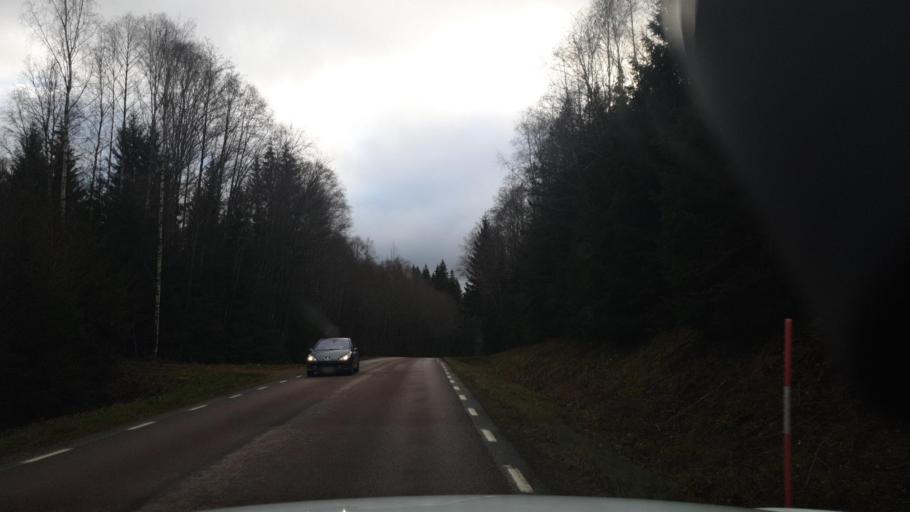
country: SE
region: Vaermland
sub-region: Arvika Kommun
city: Arvika
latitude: 59.6935
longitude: 12.7917
